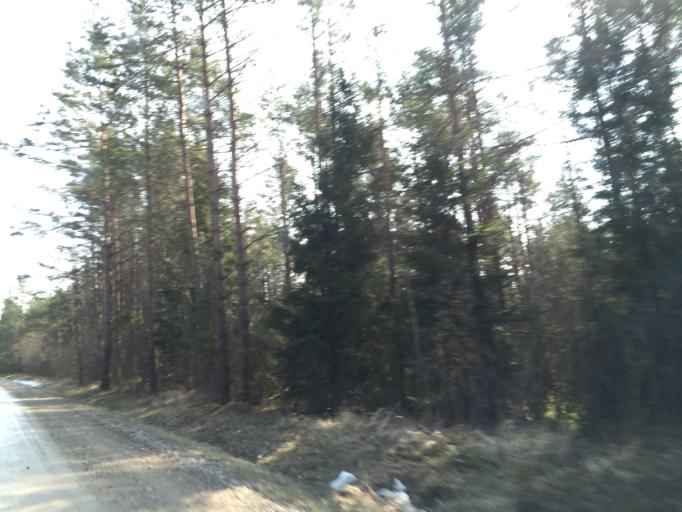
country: EE
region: Saare
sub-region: Kuressaare linn
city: Kuressaare
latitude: 58.3765
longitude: 22.7284
